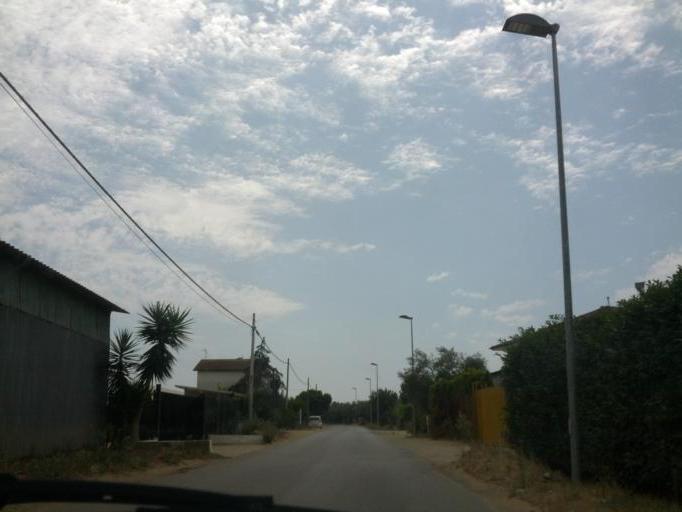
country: IT
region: Latium
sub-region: Provincia di Latina
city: Sperlonga
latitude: 41.2888
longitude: 13.3902
